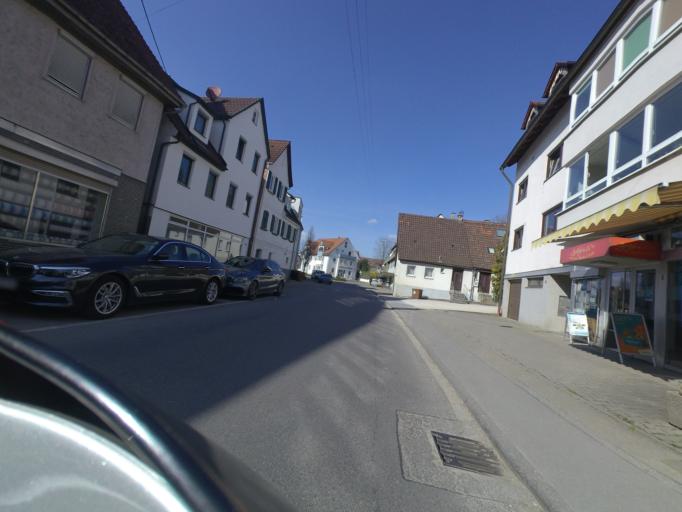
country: DE
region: Baden-Wuerttemberg
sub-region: Regierungsbezirk Stuttgart
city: Oberboihingen
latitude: 48.6495
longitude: 9.3664
